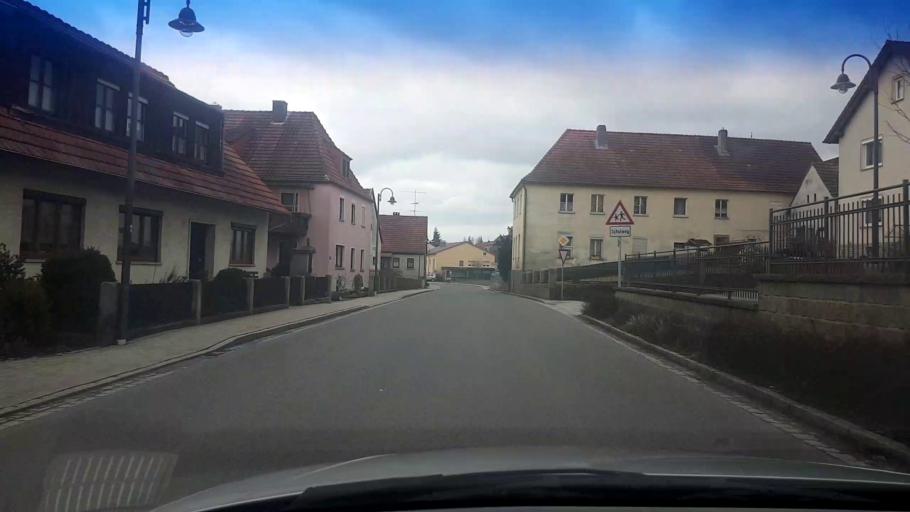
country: DE
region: Bavaria
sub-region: Regierungsbezirk Unterfranken
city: Eltmann
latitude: 49.9253
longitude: 10.6612
